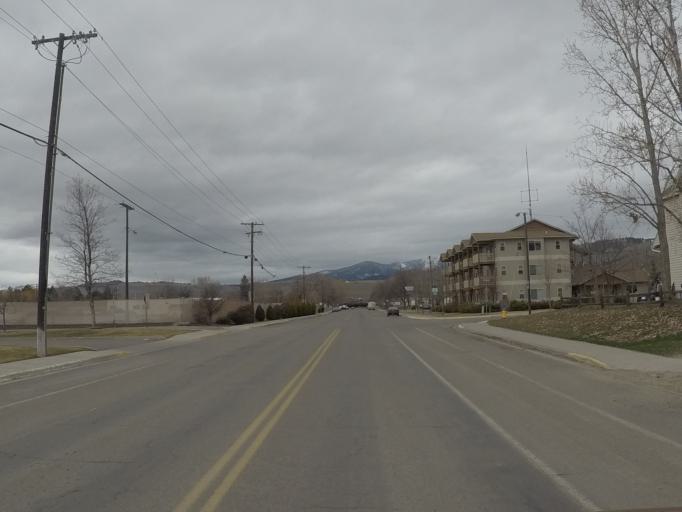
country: US
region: Montana
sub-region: Missoula County
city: Missoula
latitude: 46.8835
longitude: -114.0185
